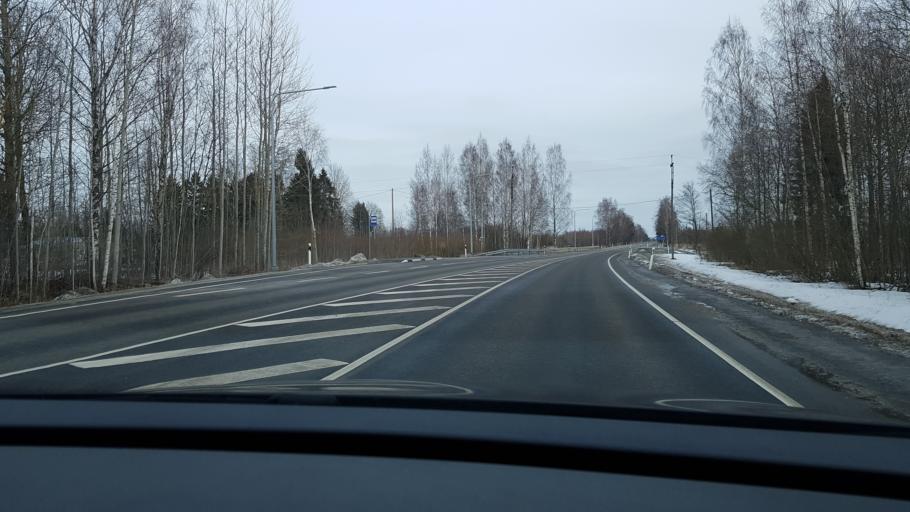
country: EE
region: Paernumaa
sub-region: Sindi linn
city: Sindi
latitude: 58.4104
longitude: 24.6738
